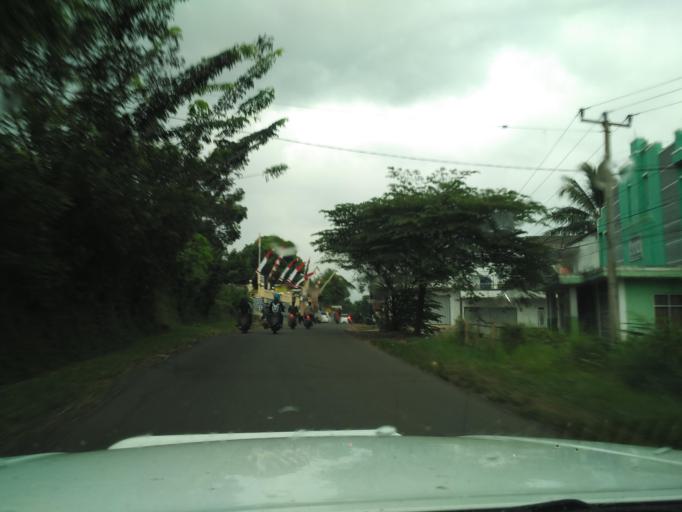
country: ID
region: West Java
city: Ciranjang-hilir
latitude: -6.7286
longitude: 107.2092
